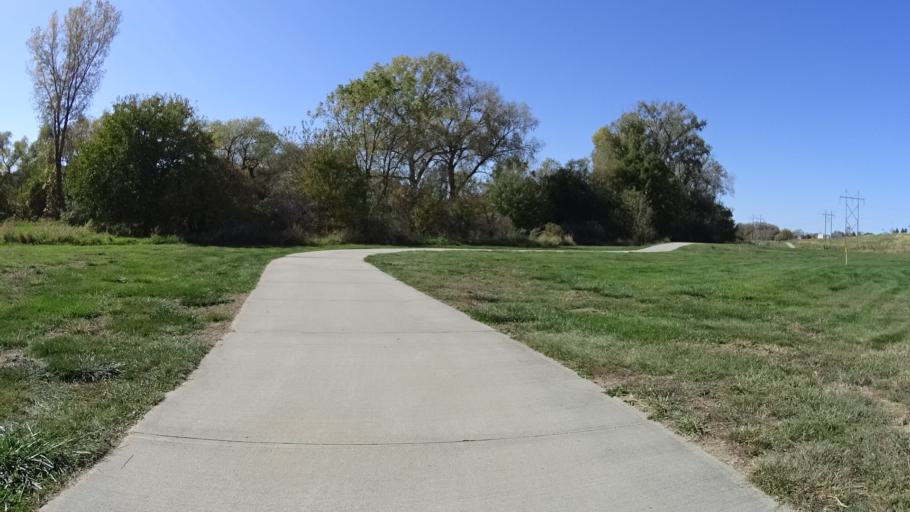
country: US
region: Nebraska
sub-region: Sarpy County
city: La Vista
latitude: 41.1682
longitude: -96.0173
